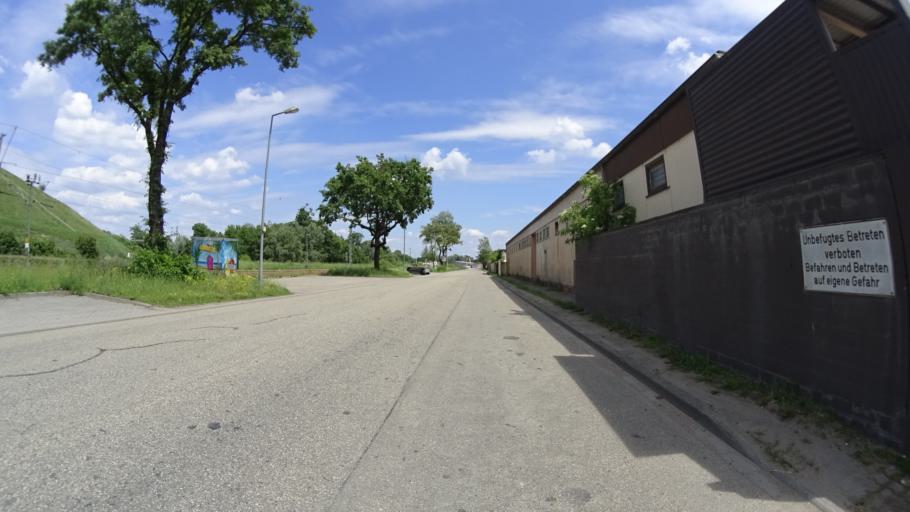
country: DE
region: Baden-Wuerttemberg
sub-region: Karlsruhe Region
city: Rheinstetten
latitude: 49.0186
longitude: 8.3364
